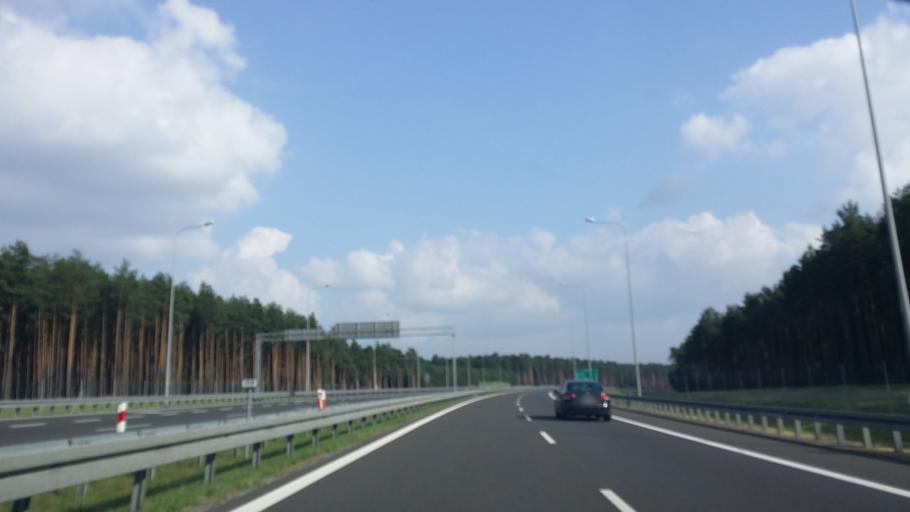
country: PL
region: Lubusz
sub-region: Powiat miedzyrzecki
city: Skwierzyna
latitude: 52.5570
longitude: 15.5339
